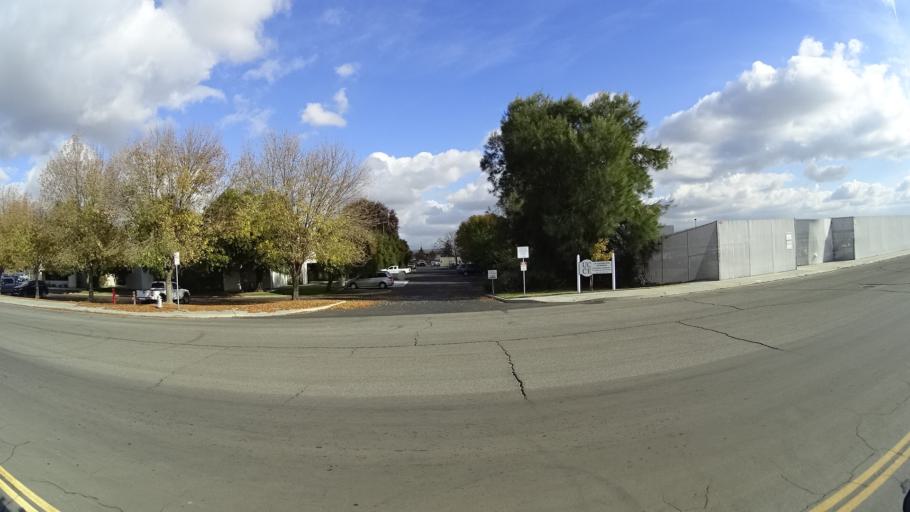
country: US
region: California
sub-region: Kern County
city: Bakersfield
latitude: 35.3458
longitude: -118.9677
